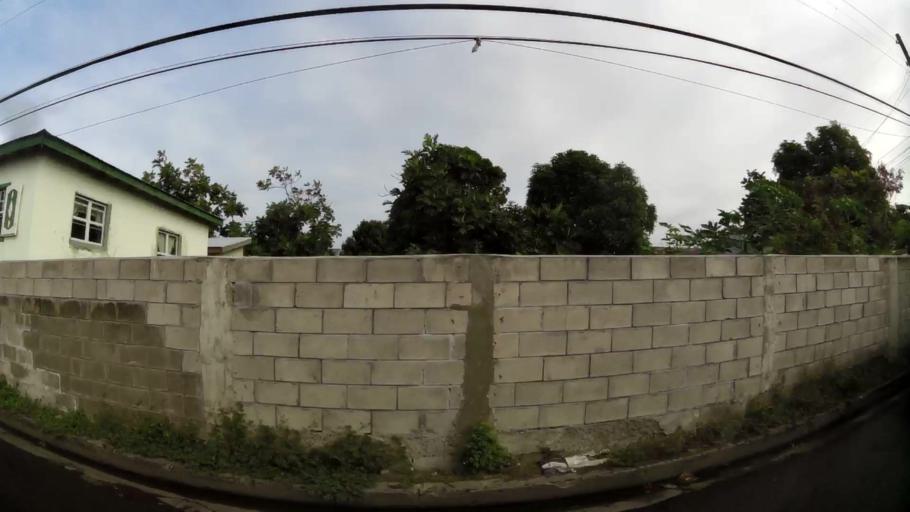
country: KN
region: Saint George Basseterre
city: Basseterre
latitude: 17.2947
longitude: -62.7185
